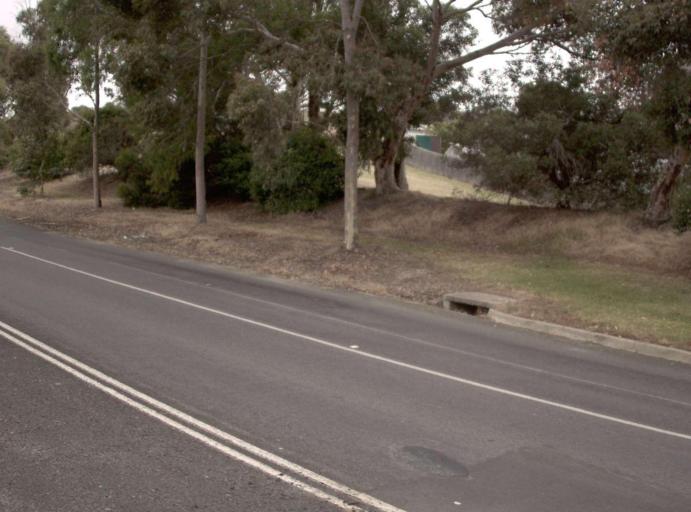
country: AU
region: Victoria
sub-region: Latrobe
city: Morwell
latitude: -38.3014
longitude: 146.4190
